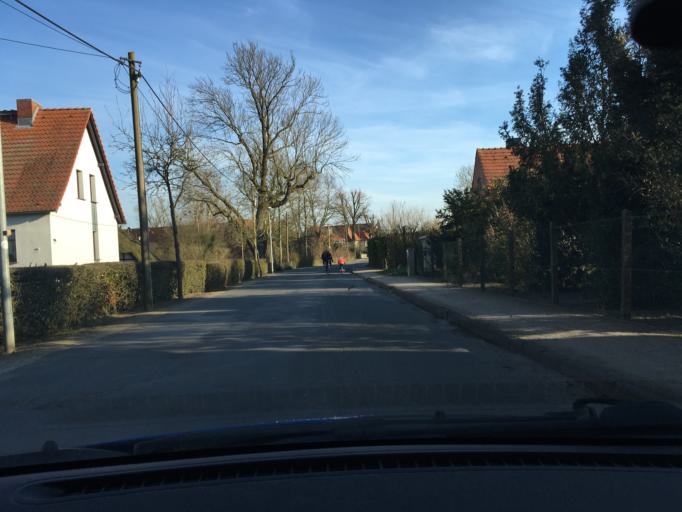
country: DE
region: Mecklenburg-Vorpommern
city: Feldstadt
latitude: 53.5975
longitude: 11.4032
